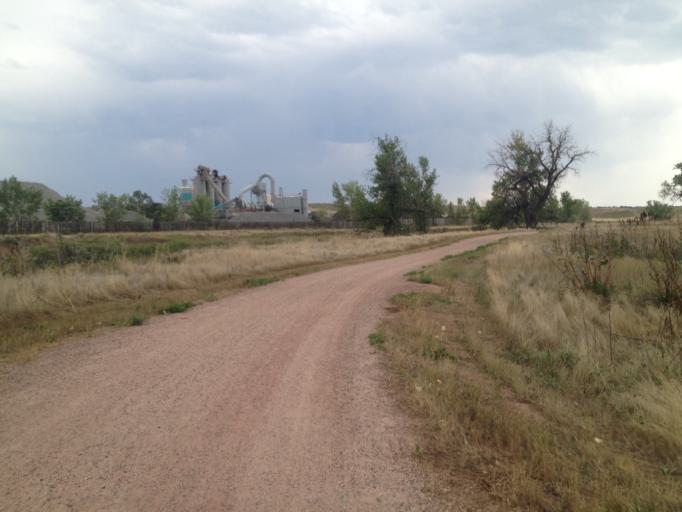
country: US
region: Colorado
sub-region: Boulder County
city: Lafayette
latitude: 39.9755
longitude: -105.0767
